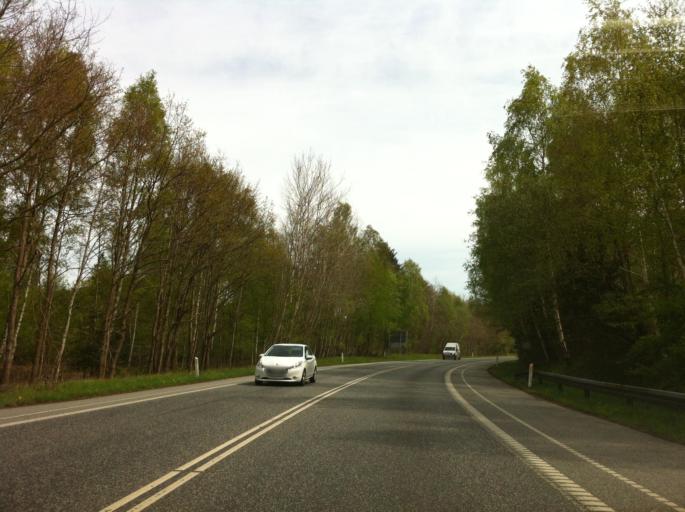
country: DK
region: Capital Region
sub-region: Allerod Kommune
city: Lillerod
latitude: 55.8697
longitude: 12.3635
